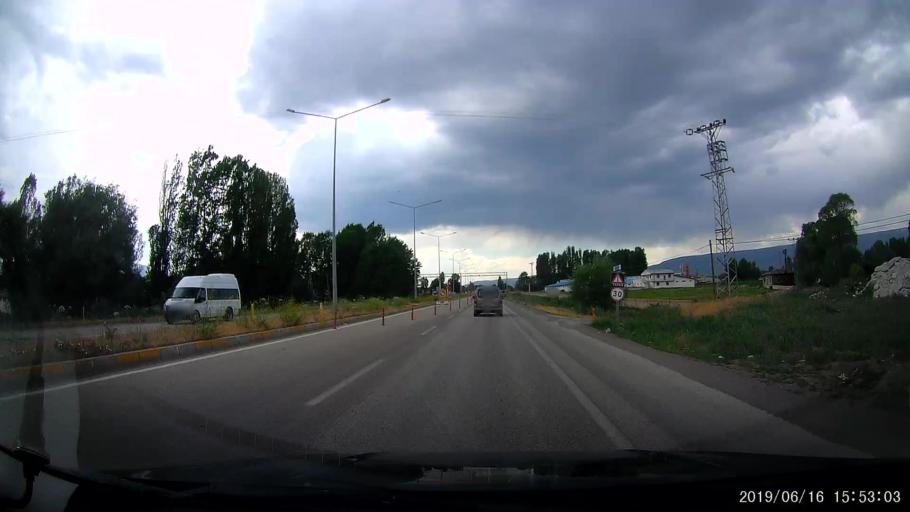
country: TR
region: Erzurum
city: Pasinler
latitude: 39.9775
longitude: 41.6519
